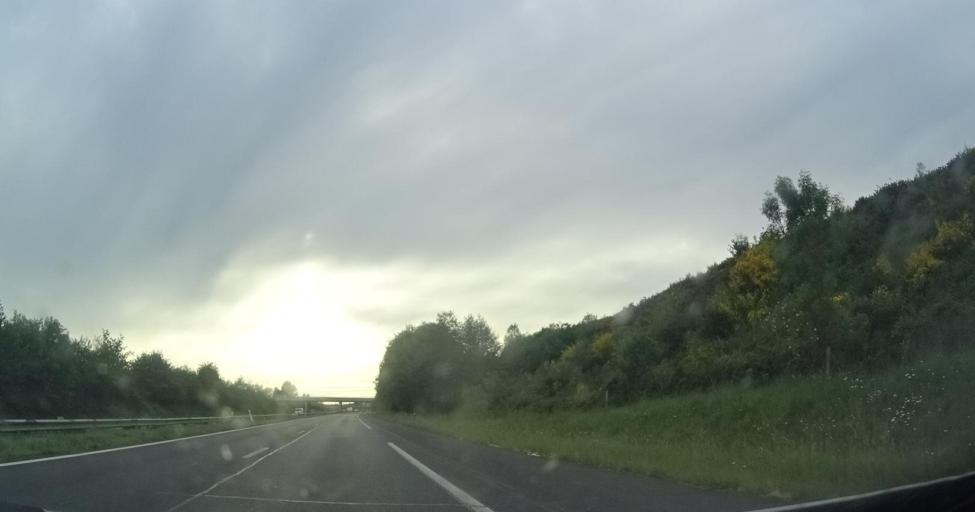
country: FR
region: Pays de la Loire
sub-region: Departement de la Loire-Atlantique
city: Sautron
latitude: 47.2546
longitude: -1.6779
